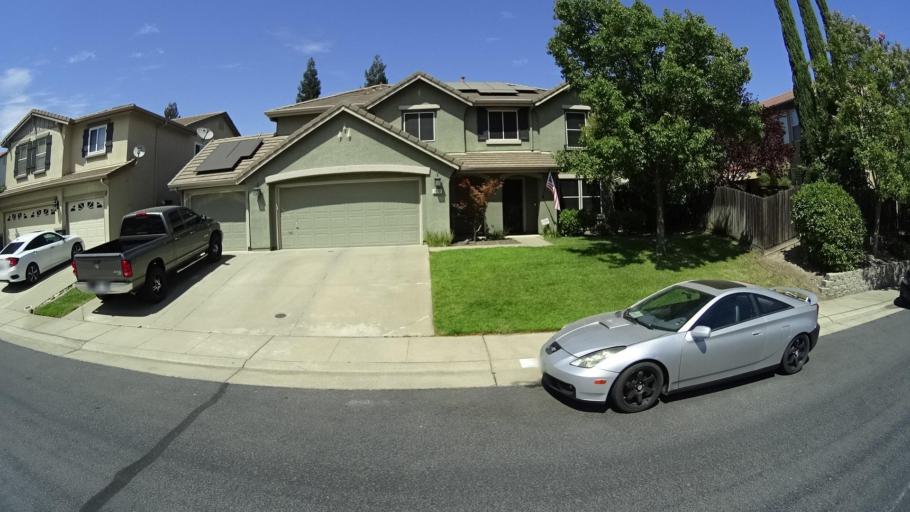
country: US
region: California
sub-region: Placer County
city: Rocklin
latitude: 38.8073
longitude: -121.2822
